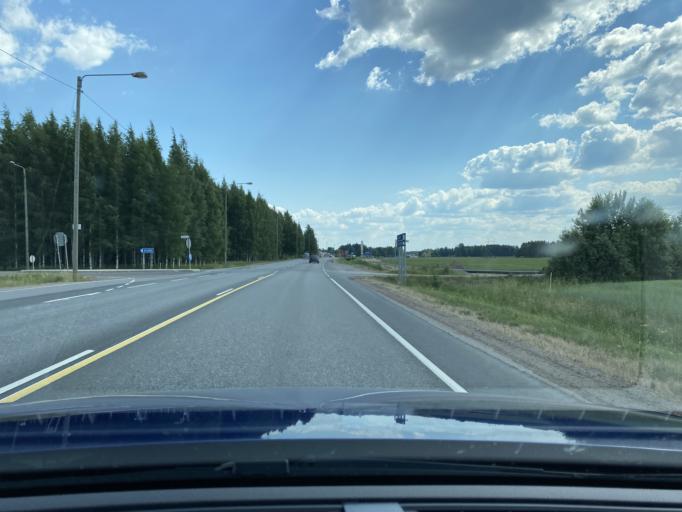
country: FI
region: Satakunta
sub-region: Rauma
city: Eura
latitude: 61.1371
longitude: 22.1193
